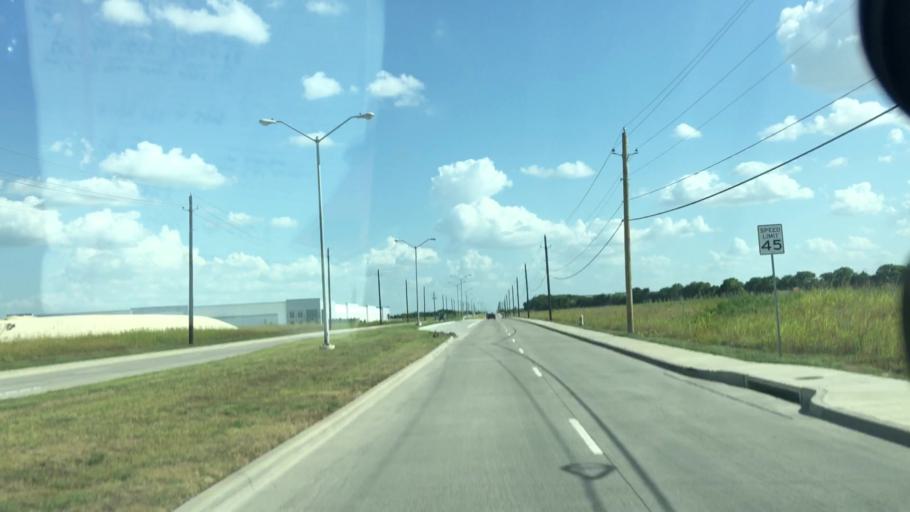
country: US
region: Texas
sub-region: Dallas County
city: Hutchins
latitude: 32.6362
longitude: -96.7521
